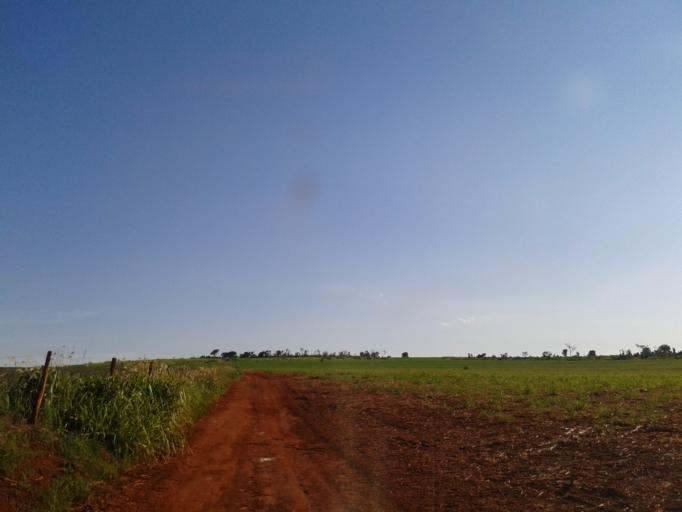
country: BR
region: Minas Gerais
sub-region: Centralina
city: Centralina
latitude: -18.6754
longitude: -49.2731
